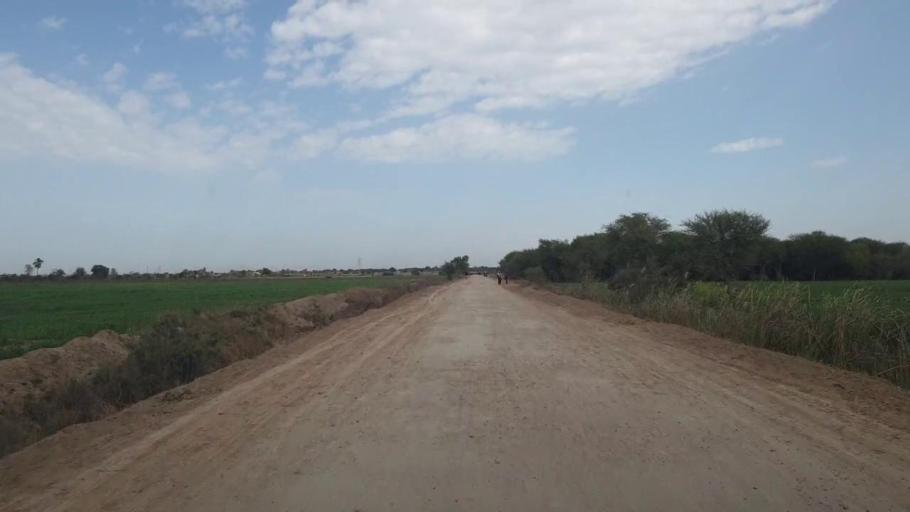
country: PK
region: Sindh
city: Sakrand
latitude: 26.0072
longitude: 68.3460
